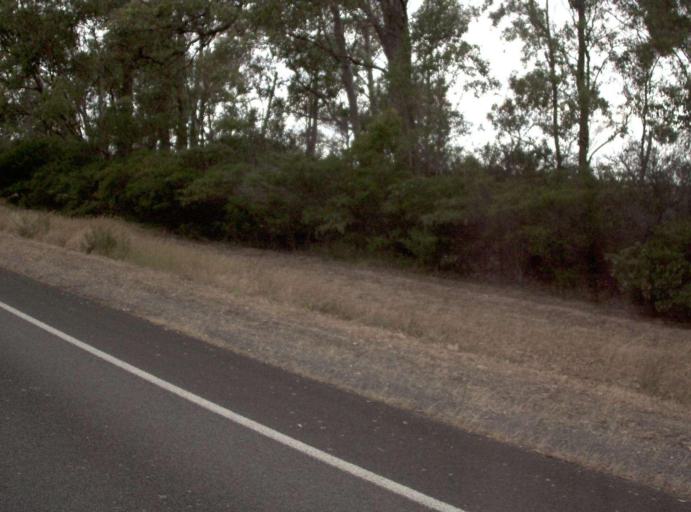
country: AU
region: Victoria
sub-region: Wellington
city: Sale
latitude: -38.4822
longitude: 146.9178
